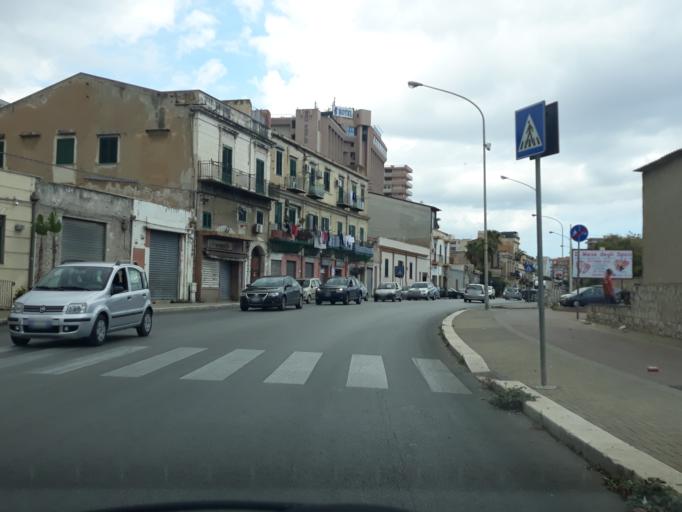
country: IT
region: Sicily
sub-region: Palermo
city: Ciaculli
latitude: 38.1069
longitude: 13.3830
